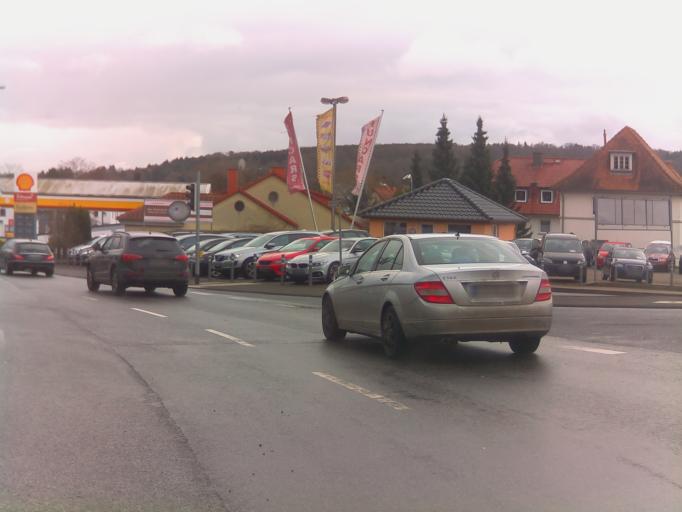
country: DE
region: Hesse
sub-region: Regierungsbezirk Giessen
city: Lauterbach
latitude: 50.6418
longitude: 9.4049
